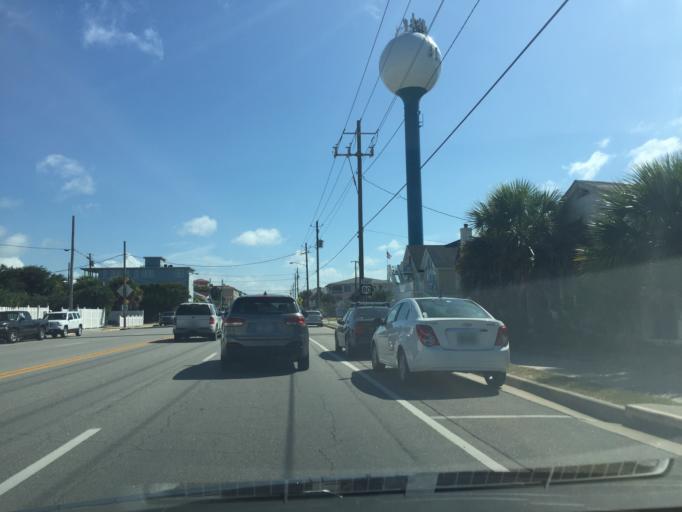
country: US
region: Georgia
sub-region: Chatham County
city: Tybee Island
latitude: 32.0120
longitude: -80.8414
